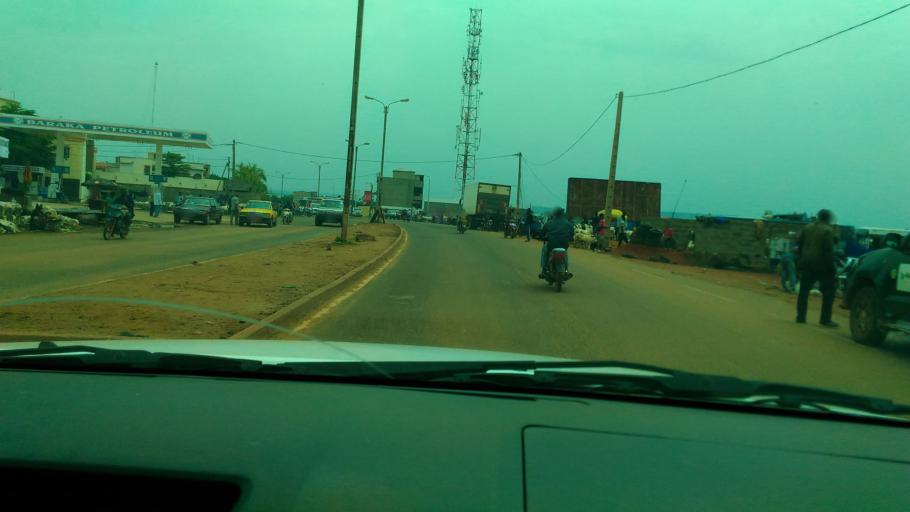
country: ML
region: Bamako
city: Bamako
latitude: 12.5770
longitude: -7.9499
